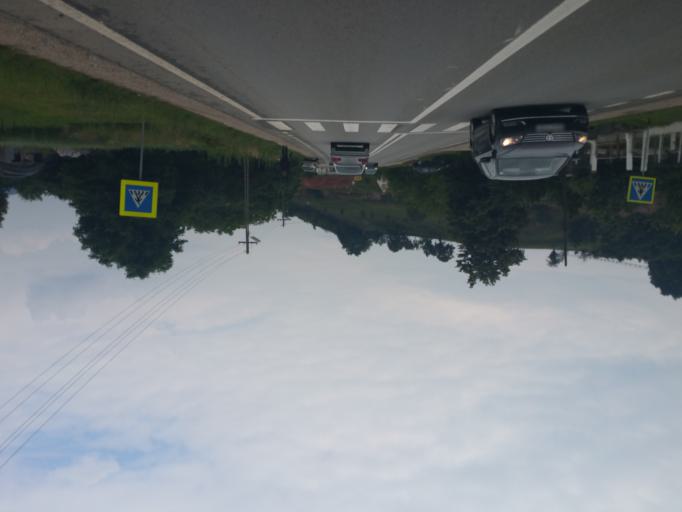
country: RO
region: Salaj
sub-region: Comuna Zimbor
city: Zimbor
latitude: 46.9990
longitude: 23.2531
